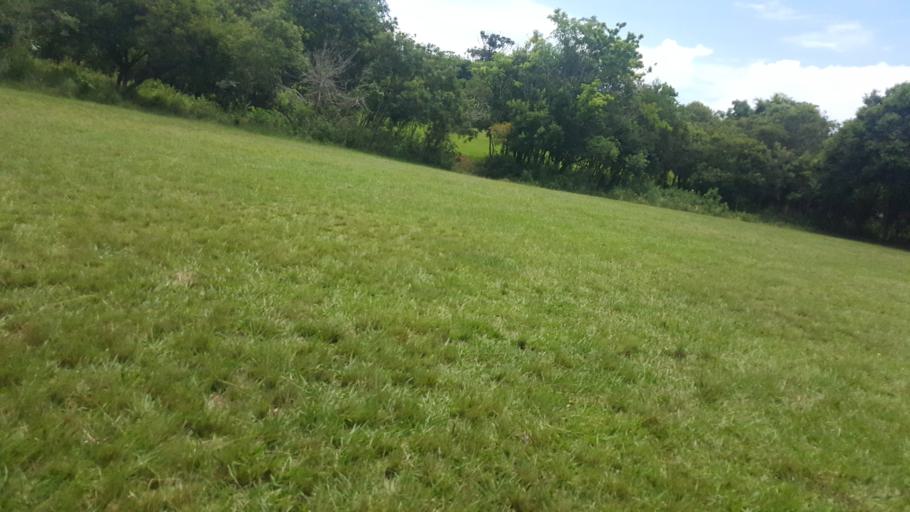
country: AR
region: Misiones
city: Capiovi
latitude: -26.9307
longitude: -55.0535
